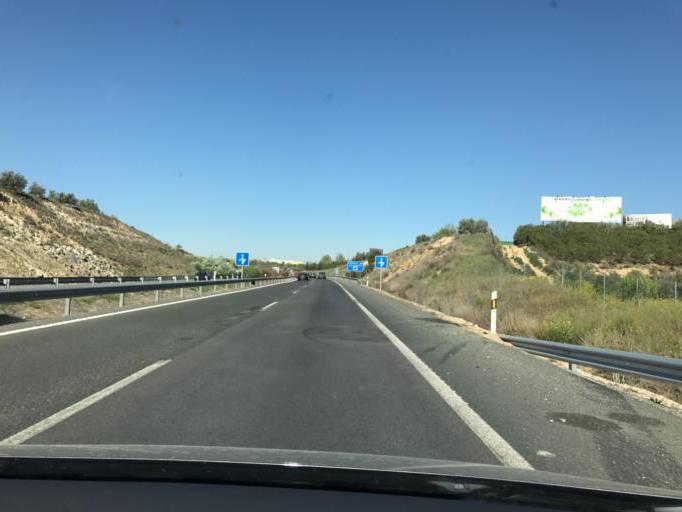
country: ES
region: Andalusia
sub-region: Provincia de Granada
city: Loja
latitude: 37.1627
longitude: -4.1139
